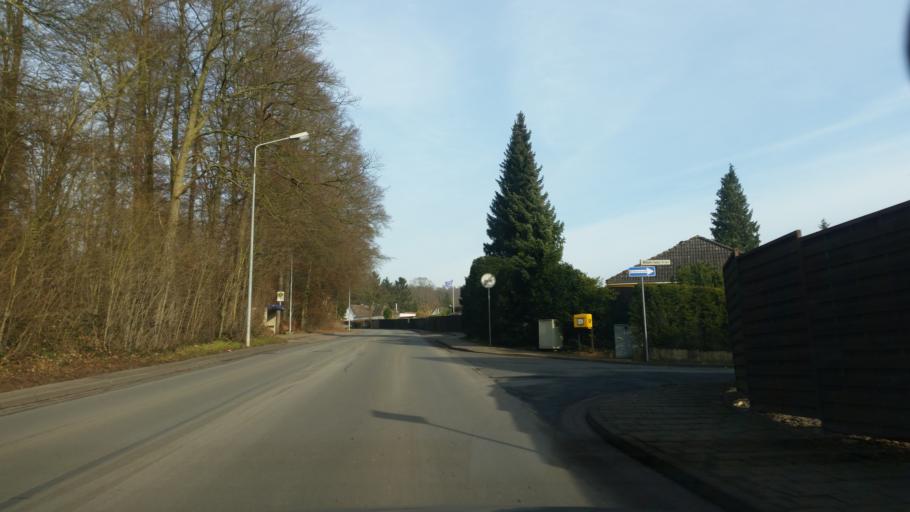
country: DE
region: Lower Saxony
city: Hameln
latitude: 52.1221
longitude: 9.3670
